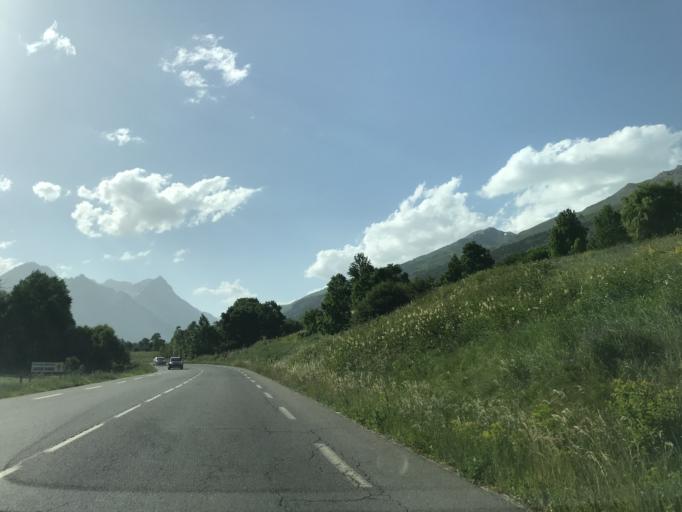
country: FR
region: Provence-Alpes-Cote d'Azur
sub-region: Departement des Hautes-Alpes
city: Villeneuve
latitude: 44.9569
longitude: 6.5469
